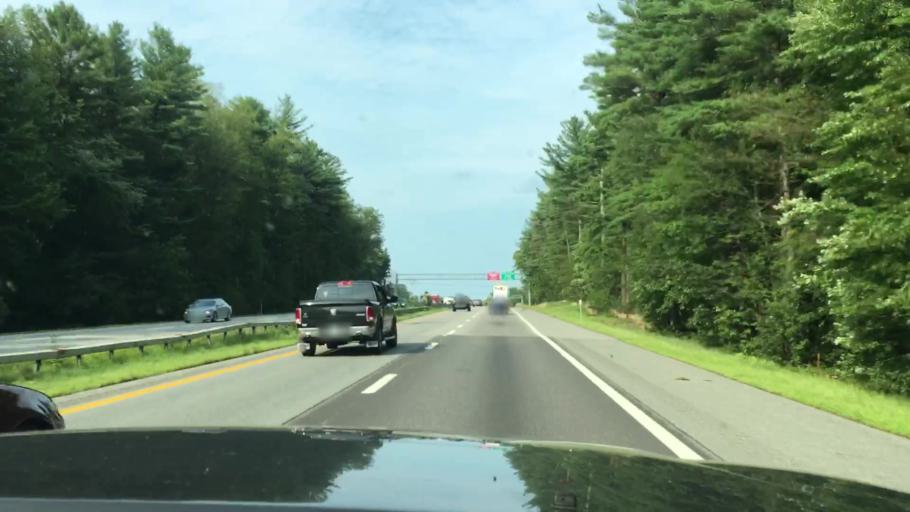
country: US
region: New Hampshire
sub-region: Hillsborough County
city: East Merrimack
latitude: 42.8968
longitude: -71.4689
